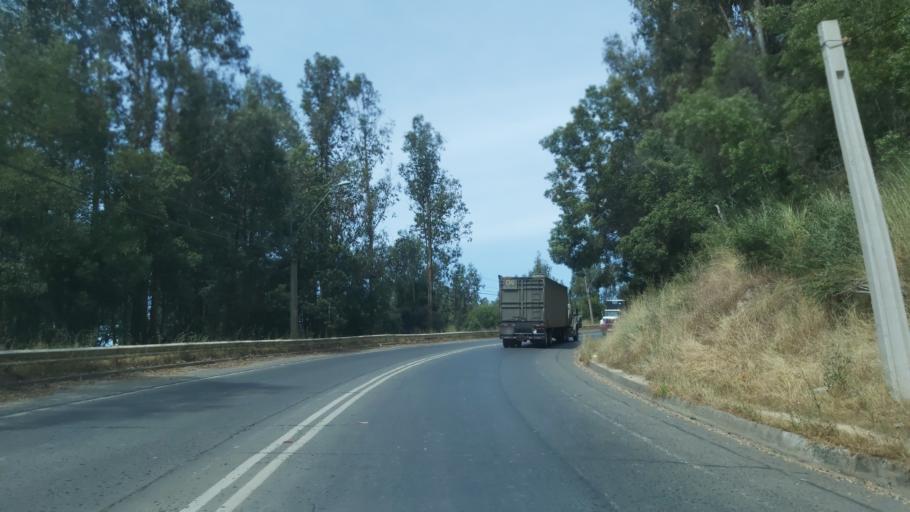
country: CL
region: Maule
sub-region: Provincia de Talca
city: Constitucion
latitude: -35.3460
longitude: -72.4150
